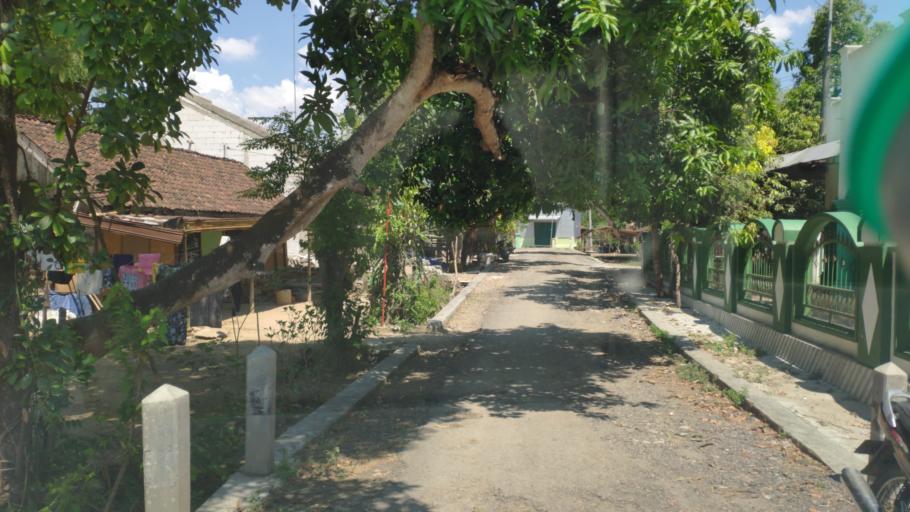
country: ID
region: Central Java
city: Galuk
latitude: -7.1086
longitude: 111.5014
